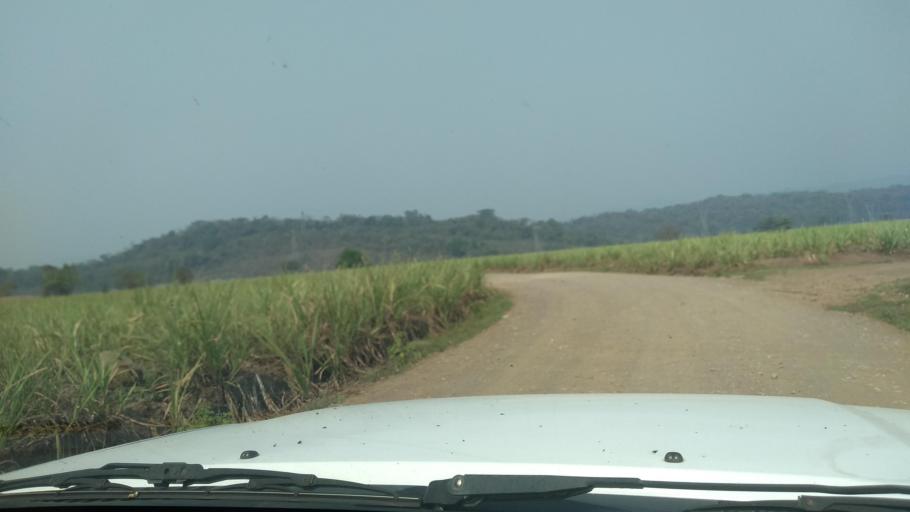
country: MX
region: Oaxaca
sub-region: Cosolapa
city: Cosolapa
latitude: 18.6184
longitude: -96.6303
